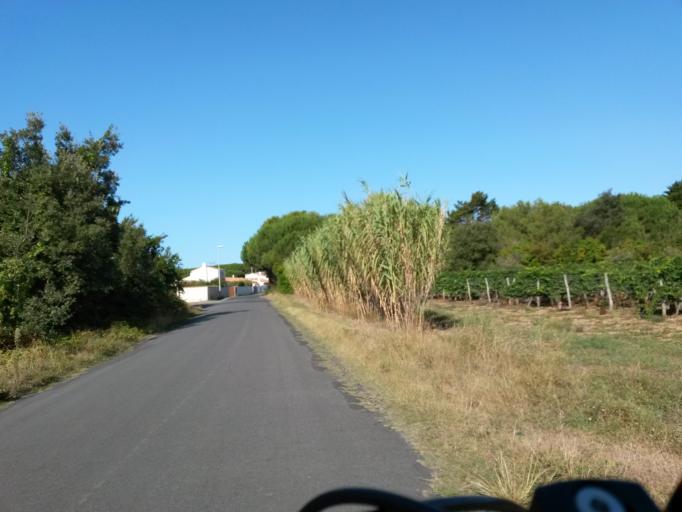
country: FR
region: Poitou-Charentes
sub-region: Departement de la Charente-Maritime
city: Sainte-Marie-de-Re
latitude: 46.1570
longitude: -1.3464
